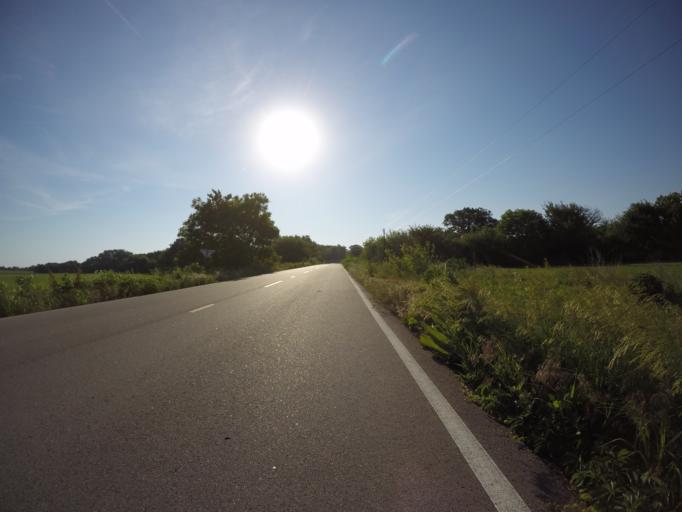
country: US
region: Nebraska
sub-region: Gage County
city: Wymore
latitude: 40.1029
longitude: -96.5047
